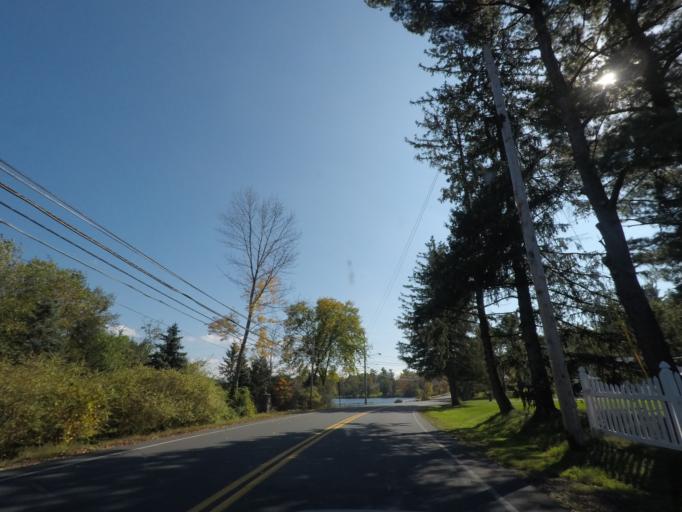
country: US
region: New York
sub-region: Rensselaer County
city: Averill Park
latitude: 42.6422
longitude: -73.5601
